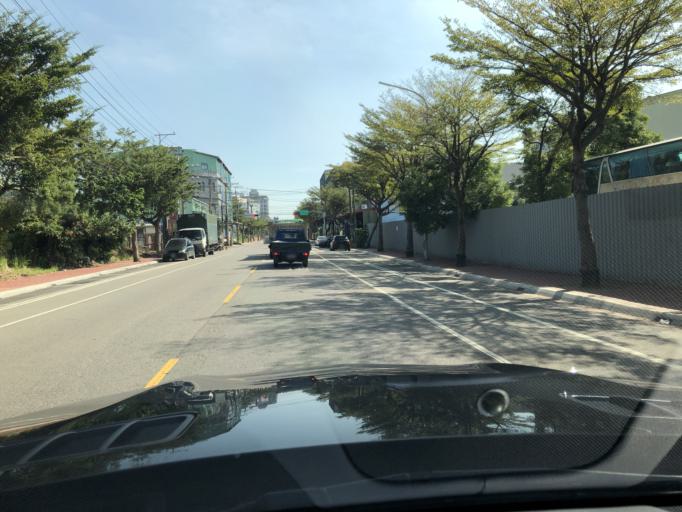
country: TW
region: Taiwan
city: Taoyuan City
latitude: 25.0714
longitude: 121.2883
